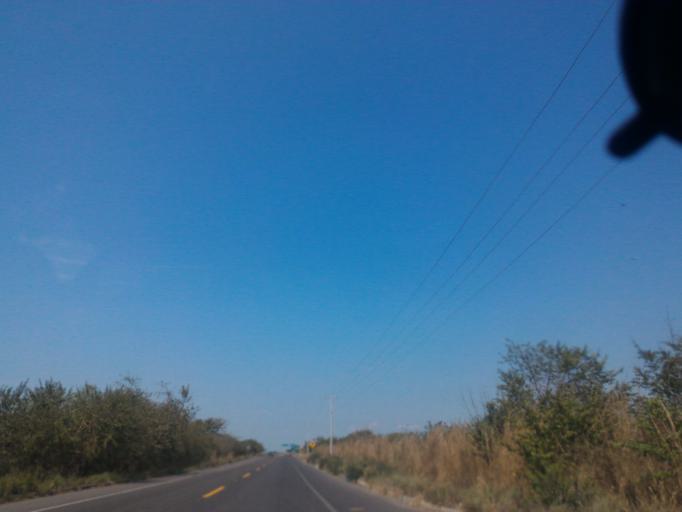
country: MX
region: Michoacan
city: Coahuayana Viejo
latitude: 18.7693
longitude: -103.7384
